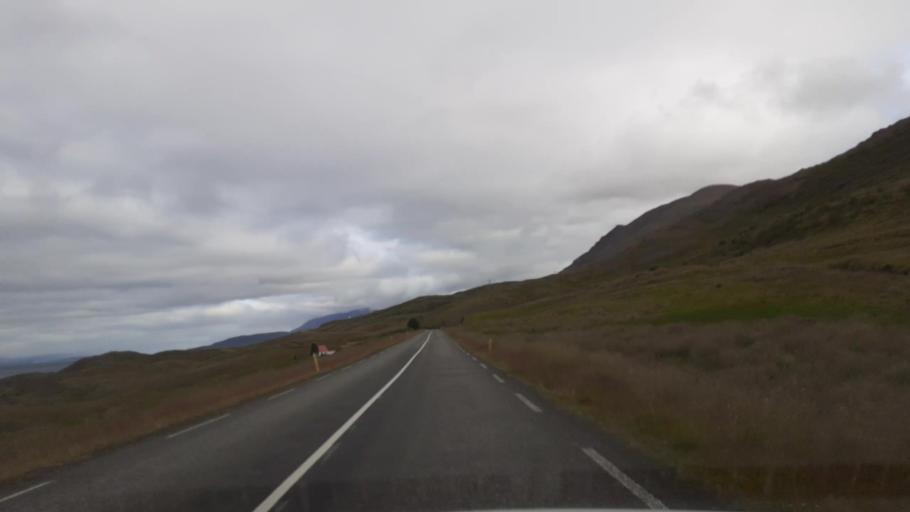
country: IS
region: Northeast
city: Akureyri
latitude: 65.8174
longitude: -18.0487
